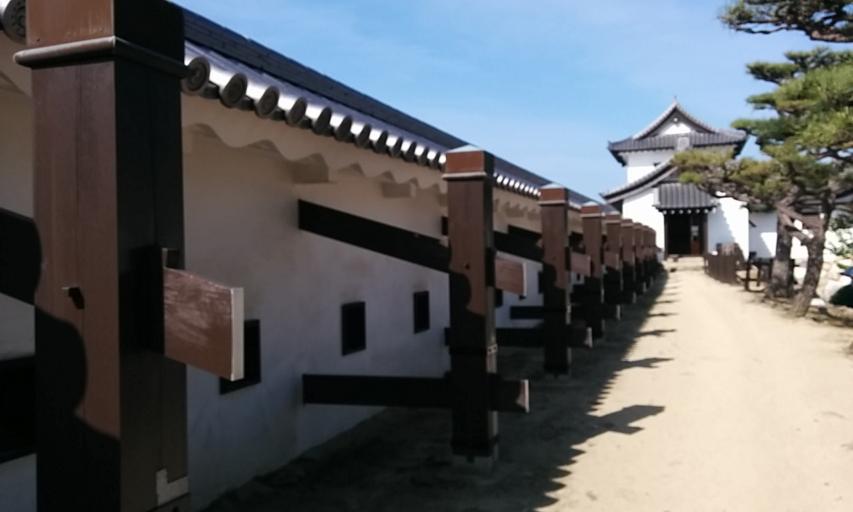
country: JP
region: Ehime
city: Saijo
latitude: 34.0641
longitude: 133.0067
